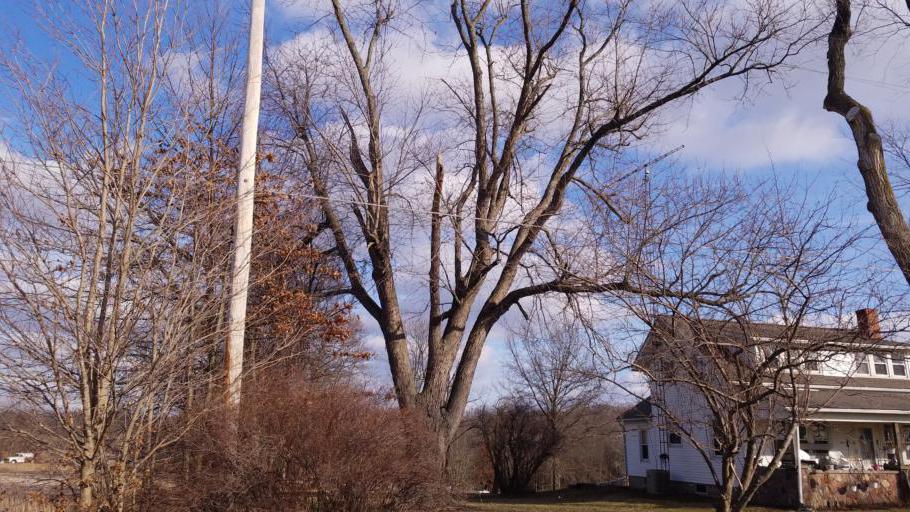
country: US
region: Ohio
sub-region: Crawford County
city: Crestline
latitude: 40.7277
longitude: -82.7033
